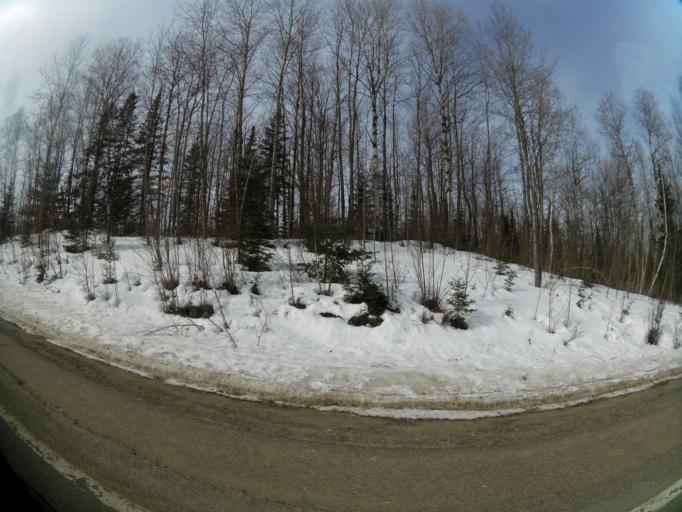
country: CA
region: Quebec
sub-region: Outaouais
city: Val-des-Monts
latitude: 45.9812
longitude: -75.5536
